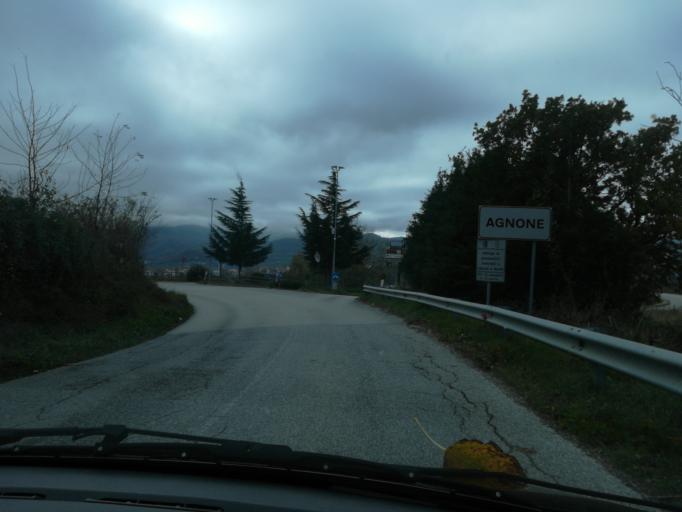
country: IT
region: Molise
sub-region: Provincia di Isernia
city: Agnone
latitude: 41.8177
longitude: 14.3724
